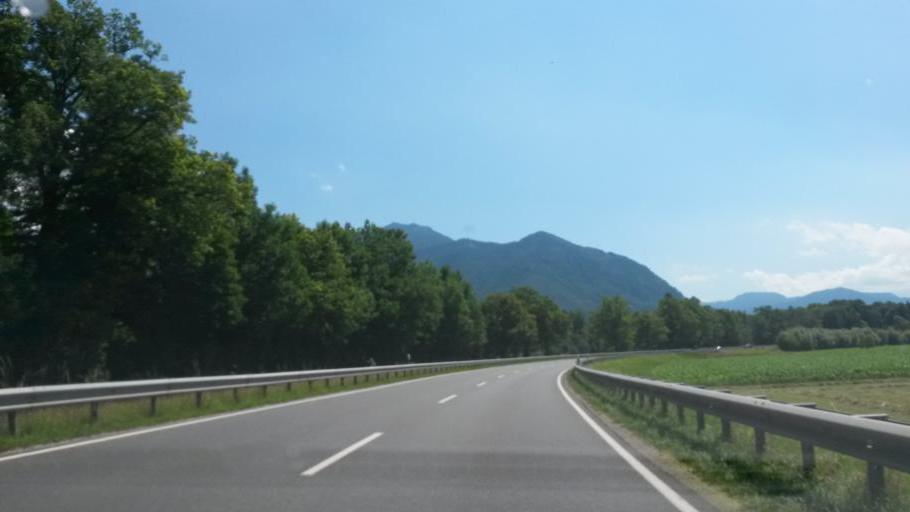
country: DE
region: Bavaria
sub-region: Upper Bavaria
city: Ubersee
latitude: 47.8014
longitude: 12.4902
